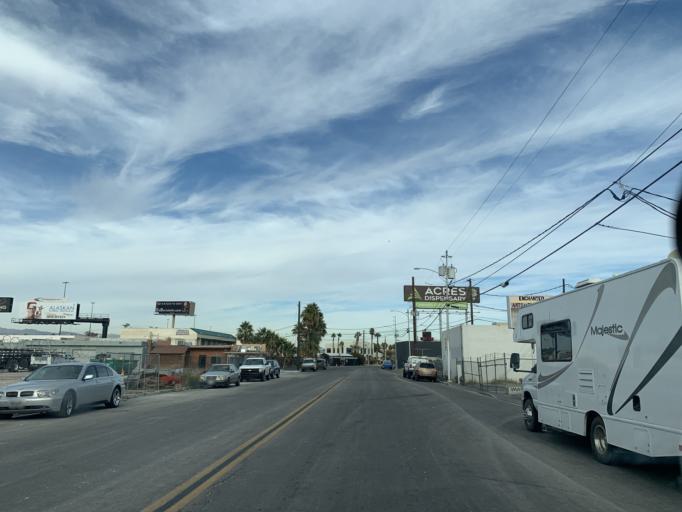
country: US
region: Nevada
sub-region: Clark County
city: Las Vegas
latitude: 36.1454
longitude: -115.1683
